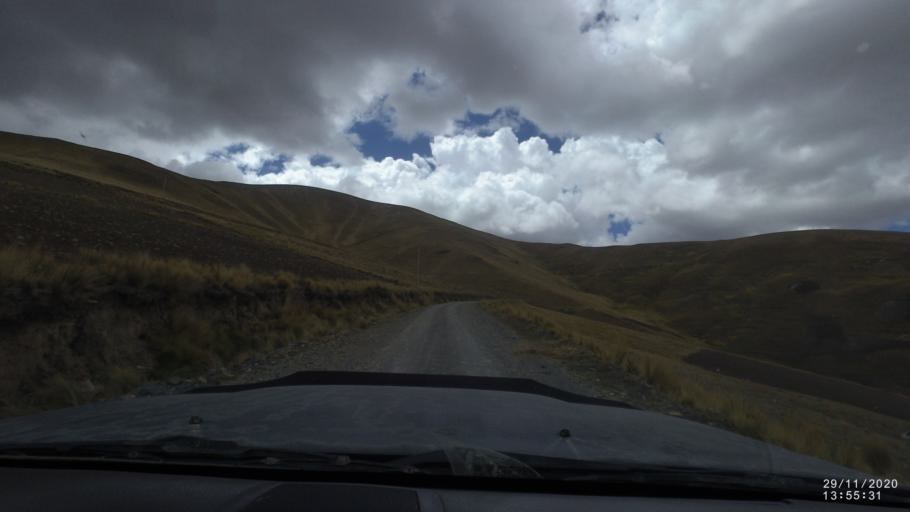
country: BO
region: Cochabamba
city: Sipe Sipe
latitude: -17.1751
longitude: -66.3578
